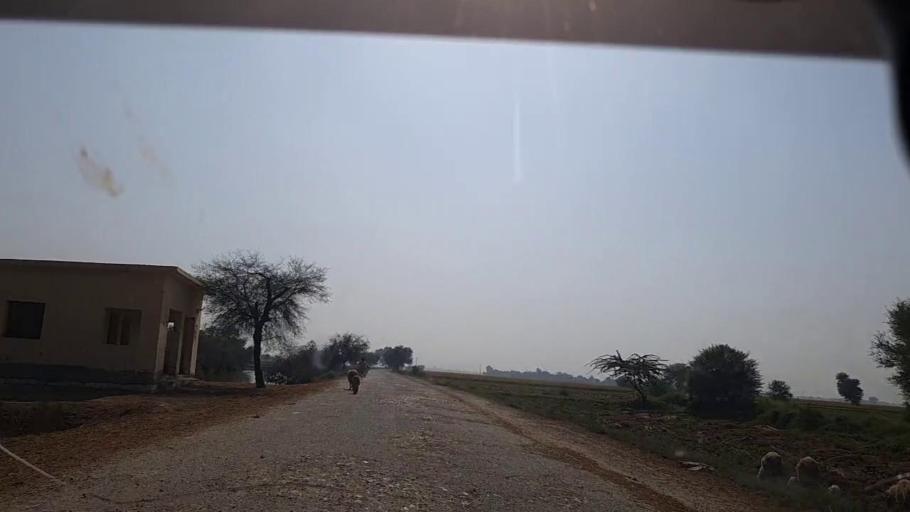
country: PK
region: Sindh
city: Shikarpur
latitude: 28.0972
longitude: 68.6109
